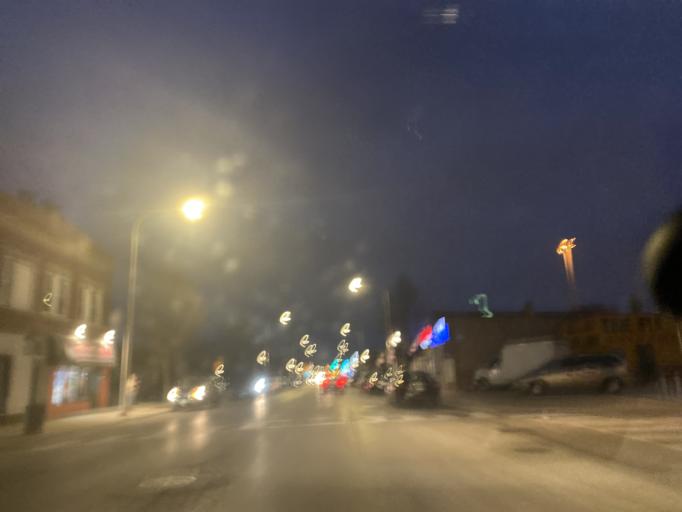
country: US
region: Illinois
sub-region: Cook County
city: Chicago
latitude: 41.7795
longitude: -87.6570
